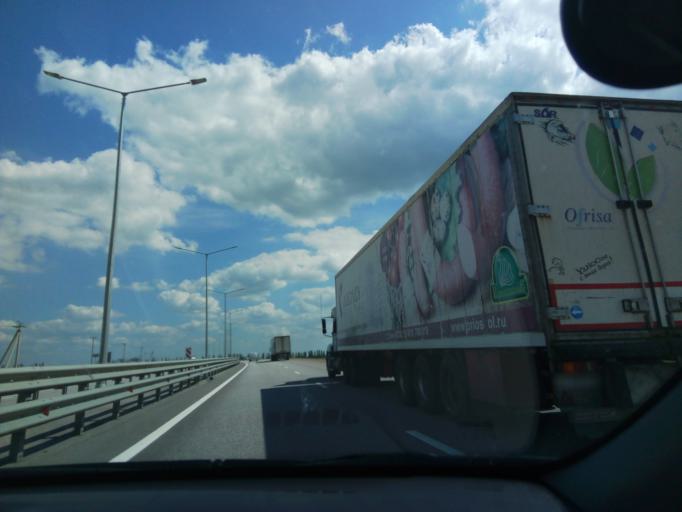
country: RU
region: Voronezj
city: Kashirskoye
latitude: 51.4883
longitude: 39.5328
